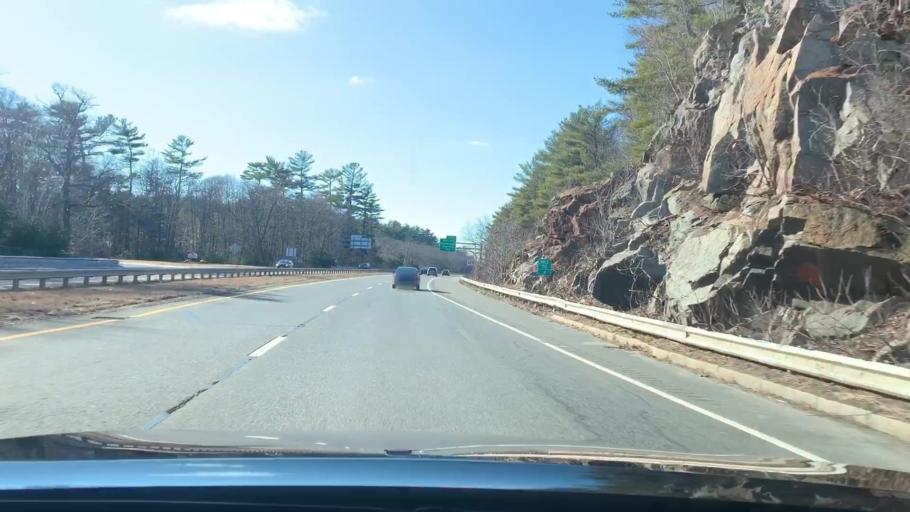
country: US
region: Massachusetts
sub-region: Essex County
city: Essex
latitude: 42.5902
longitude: -70.7654
